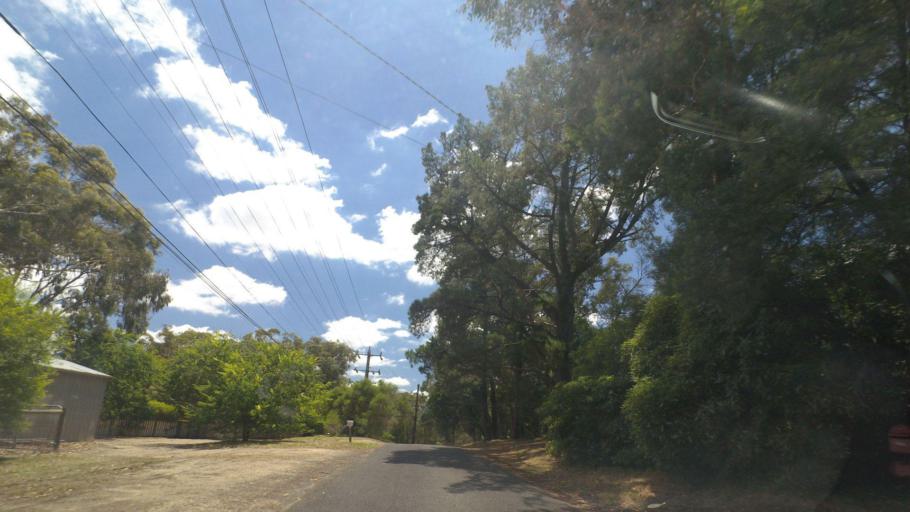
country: AU
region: Victoria
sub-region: Manningham
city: Warrandyte
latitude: -37.7396
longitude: 145.2567
